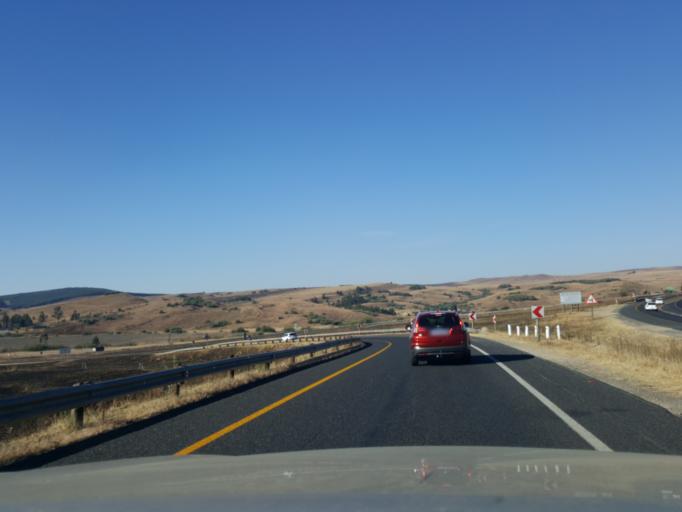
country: ZA
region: Mpumalanga
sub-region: Nkangala District Municipality
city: Belfast
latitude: -25.6120
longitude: 30.2770
